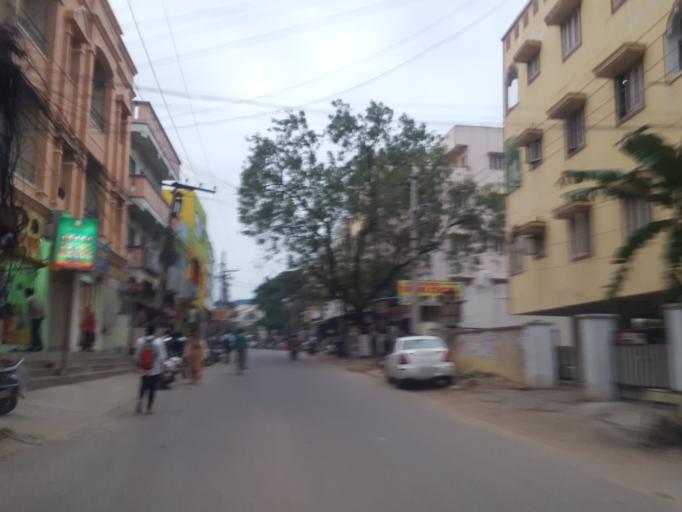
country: IN
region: Telangana
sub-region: Medak
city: Serilingampalle
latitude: 17.4935
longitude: 78.3319
